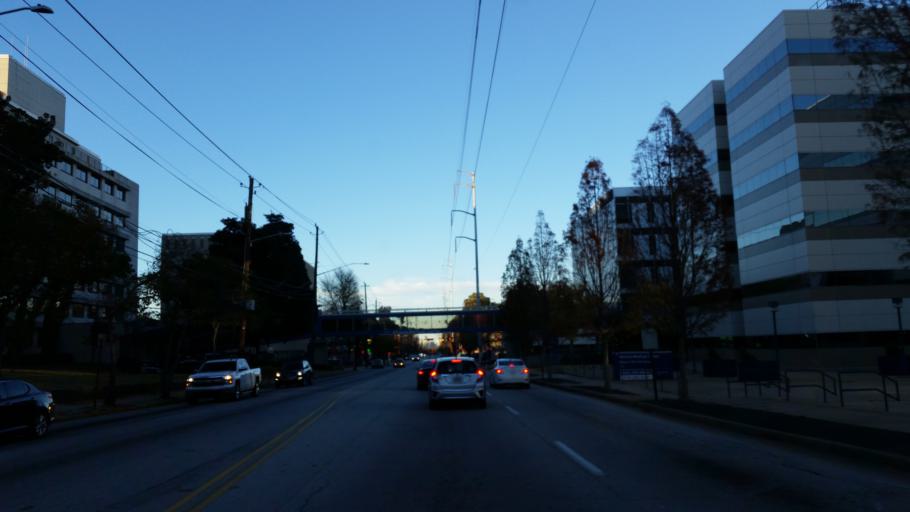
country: US
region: Georgia
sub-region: Fulton County
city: Atlanta
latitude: 33.7622
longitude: -84.3720
